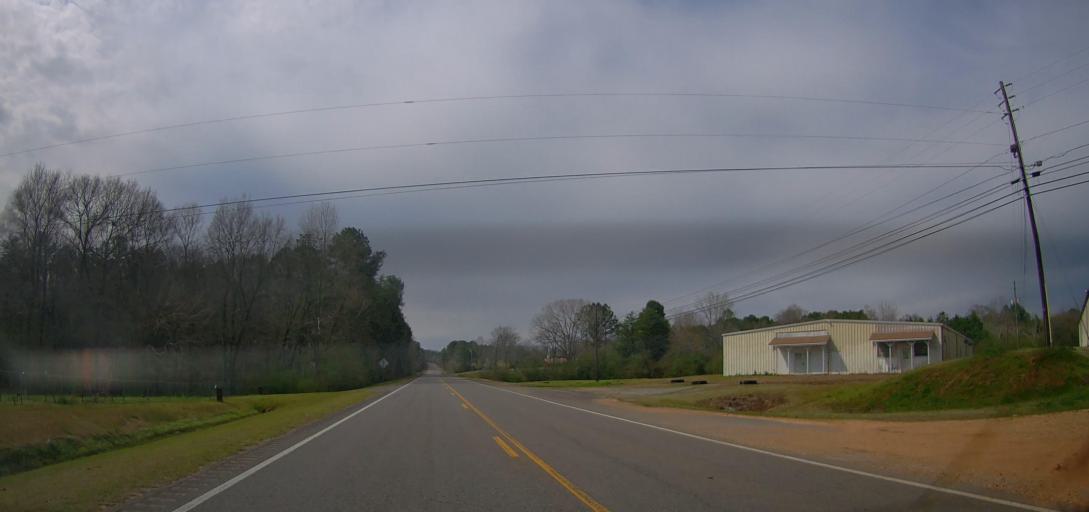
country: US
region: Alabama
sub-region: Walker County
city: Carbon Hill
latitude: 33.9063
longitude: -87.5531
